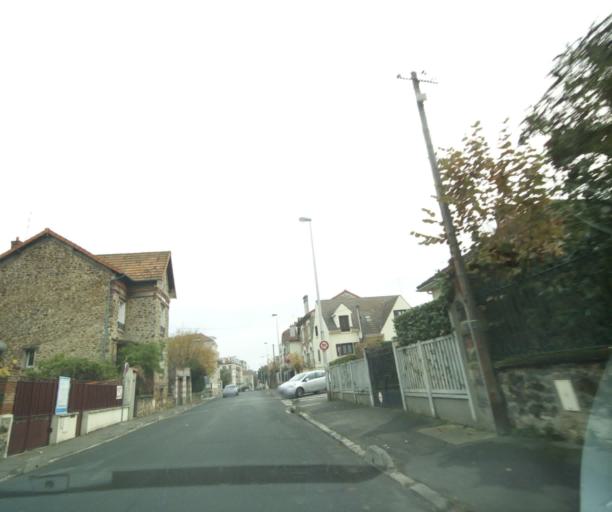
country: FR
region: Ile-de-France
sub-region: Departement de Seine-Saint-Denis
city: Villemomble
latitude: 48.8871
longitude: 2.5070
